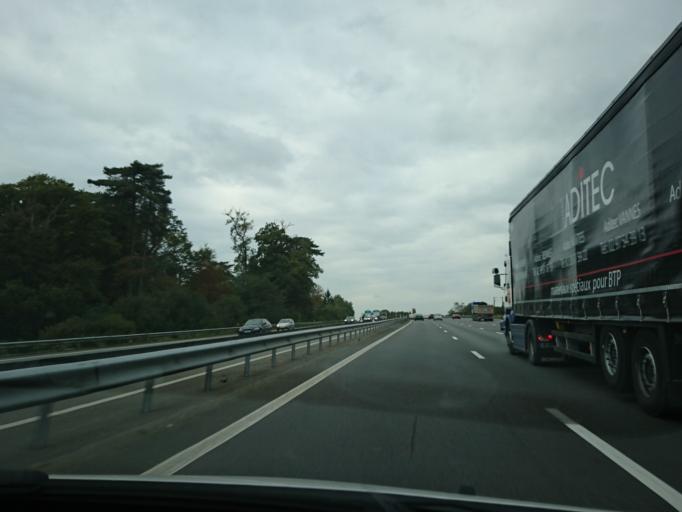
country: FR
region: Pays de la Loire
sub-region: Departement de la Loire-Atlantique
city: Savenay
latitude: 47.3656
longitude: -1.9064
